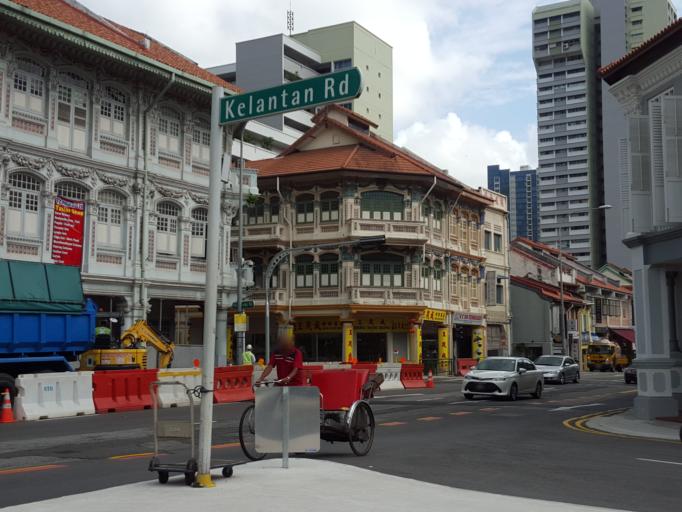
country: SG
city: Singapore
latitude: 1.3061
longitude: 103.8558
